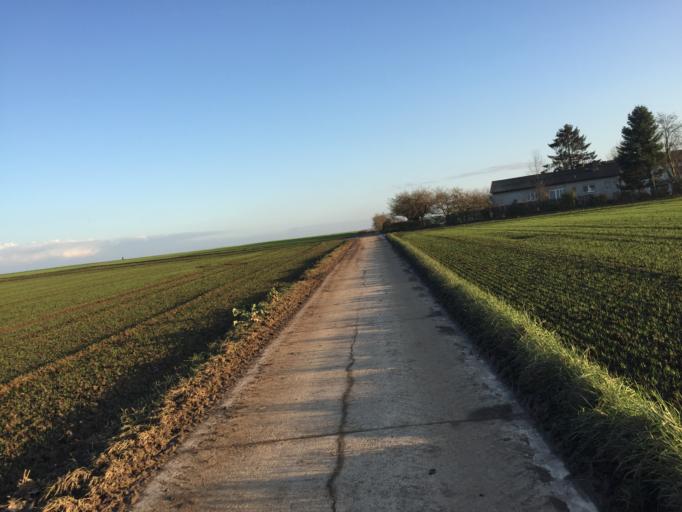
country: DE
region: Hesse
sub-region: Regierungsbezirk Darmstadt
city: Munzenberg
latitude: 50.4834
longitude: 8.7441
